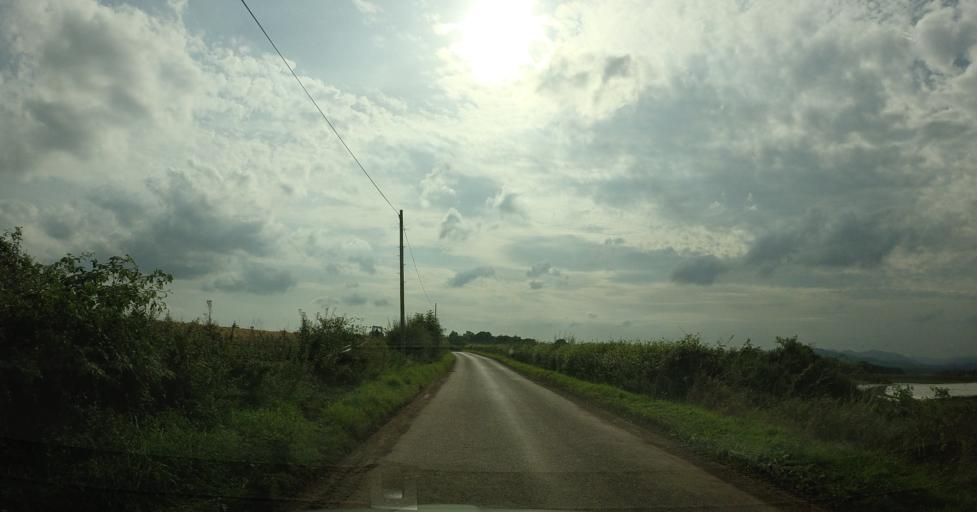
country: GB
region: Scotland
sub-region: Perth and Kinross
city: Auchterarder
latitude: 56.3537
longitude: -3.7183
